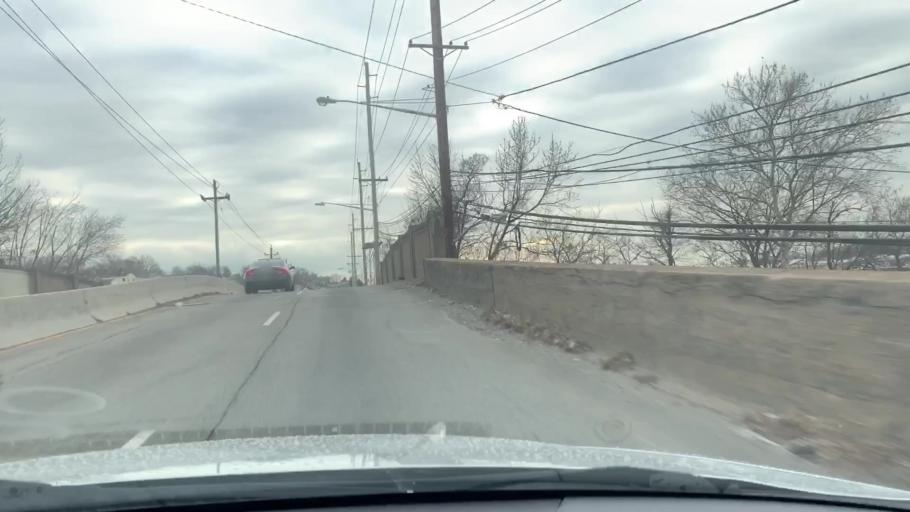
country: US
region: New Jersey
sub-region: Bergen County
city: Fairview
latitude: 40.8160
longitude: -74.0085
